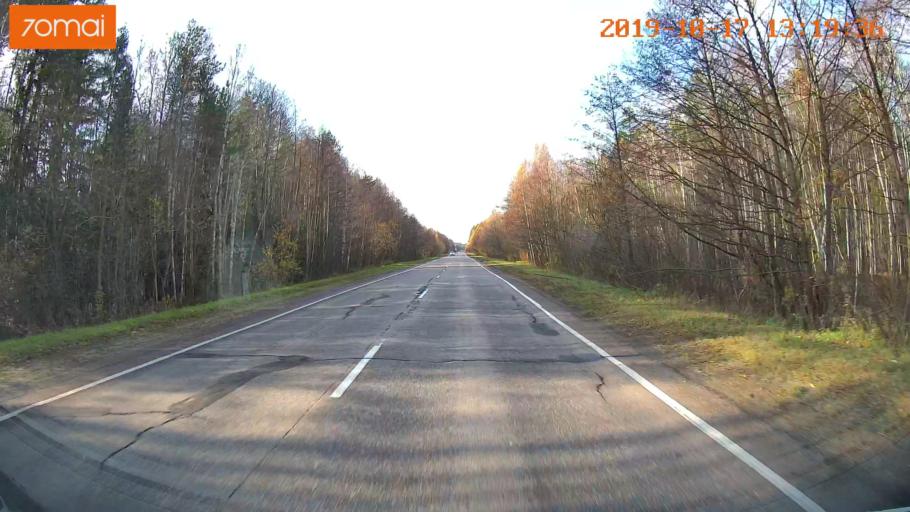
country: RU
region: Rjazan
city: Gus'-Zheleznyy
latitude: 55.0705
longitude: 41.0701
